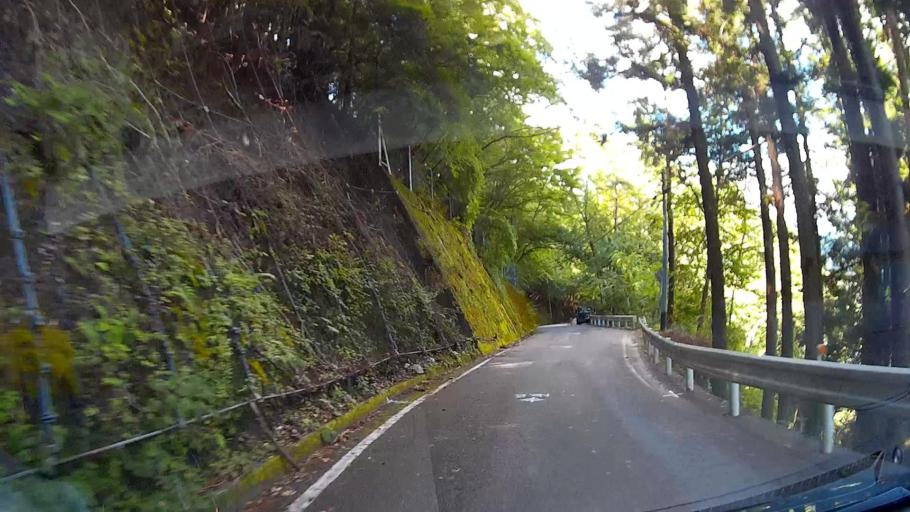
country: JP
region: Shizuoka
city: Shizuoka-shi
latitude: 35.2068
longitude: 138.2350
